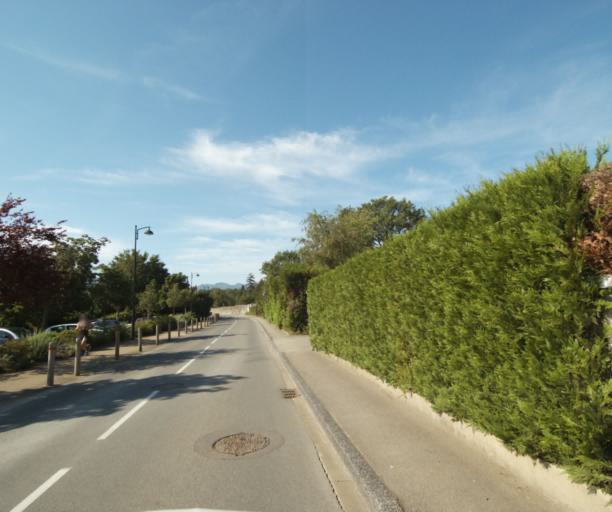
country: FR
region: Rhone-Alpes
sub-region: Departement de la Haute-Savoie
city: Marin
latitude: 46.3956
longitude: 6.5031
